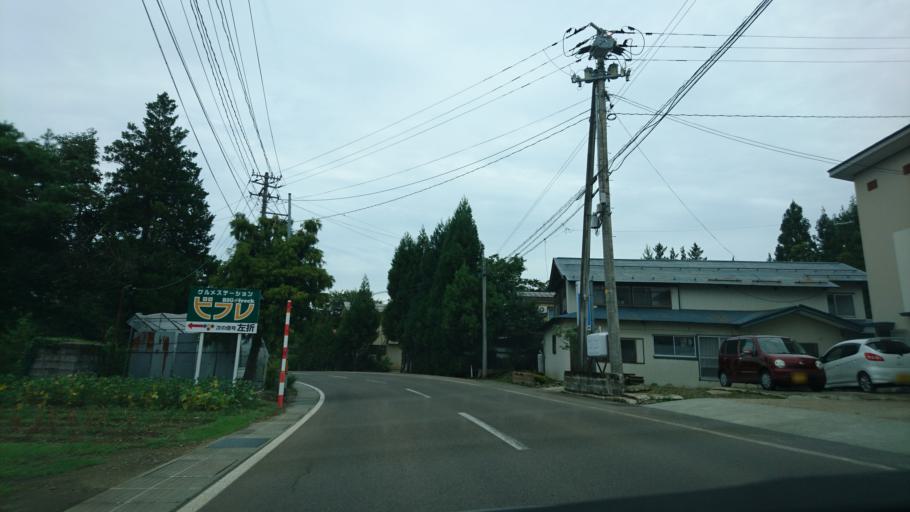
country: JP
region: Akita
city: Yuzawa
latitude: 39.1517
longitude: 140.5699
